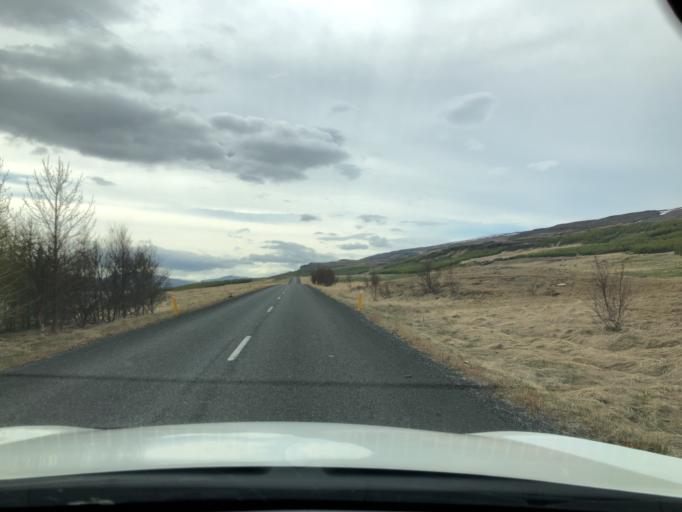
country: IS
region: East
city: Egilsstadir
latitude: 65.1691
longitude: -14.6839
